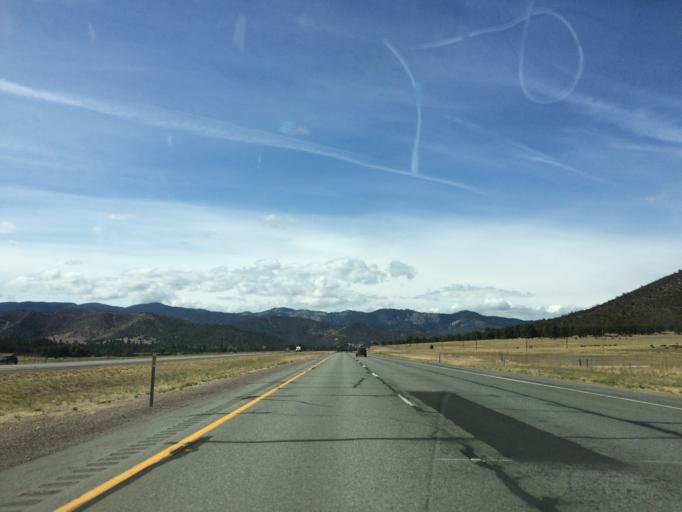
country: US
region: California
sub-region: Siskiyou County
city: Yreka
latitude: 41.6706
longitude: -122.6147
